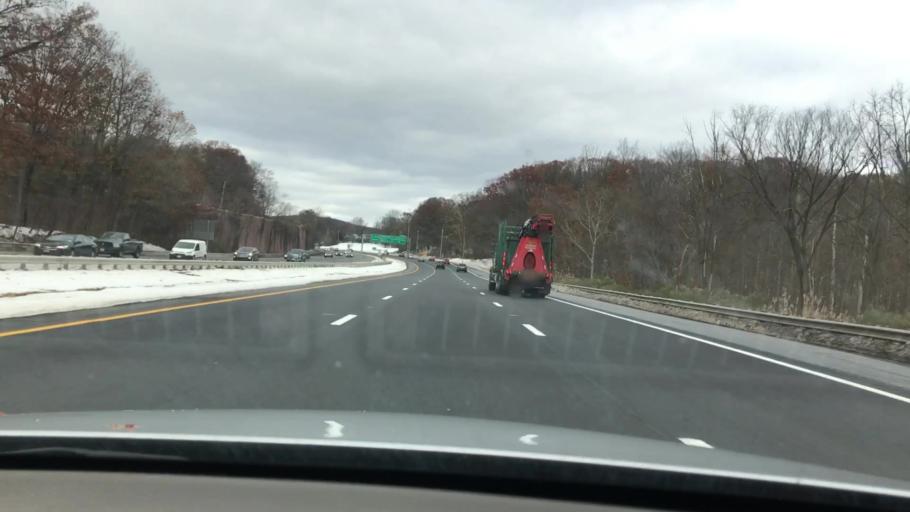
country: US
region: New Jersey
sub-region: Morris County
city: Mountain Lakes
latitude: 40.8870
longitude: -74.4167
